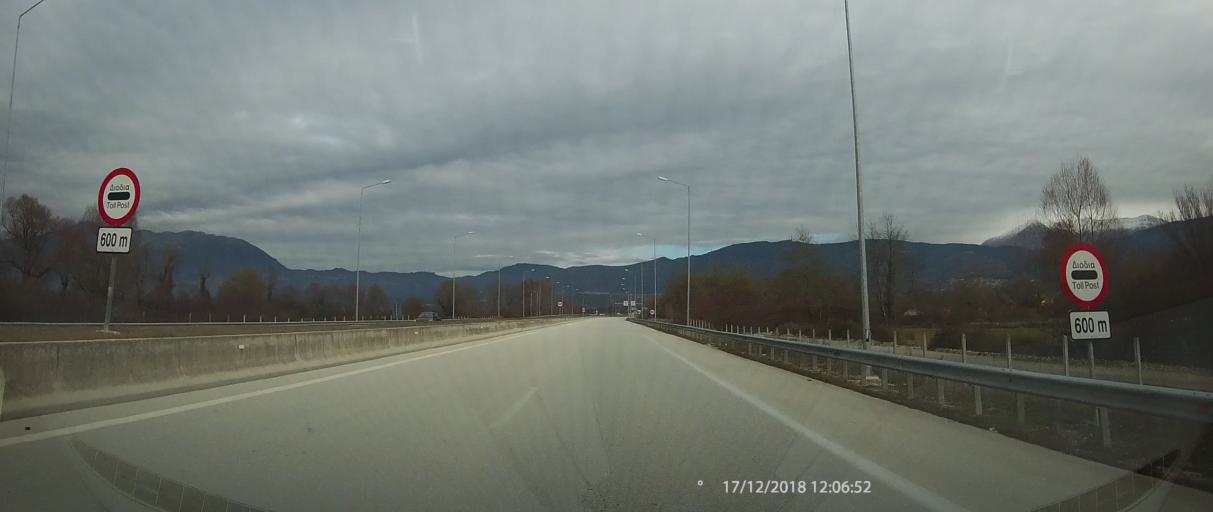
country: GR
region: Epirus
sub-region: Nomos Ioanninon
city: Koutselio
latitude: 39.6132
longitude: 20.9428
